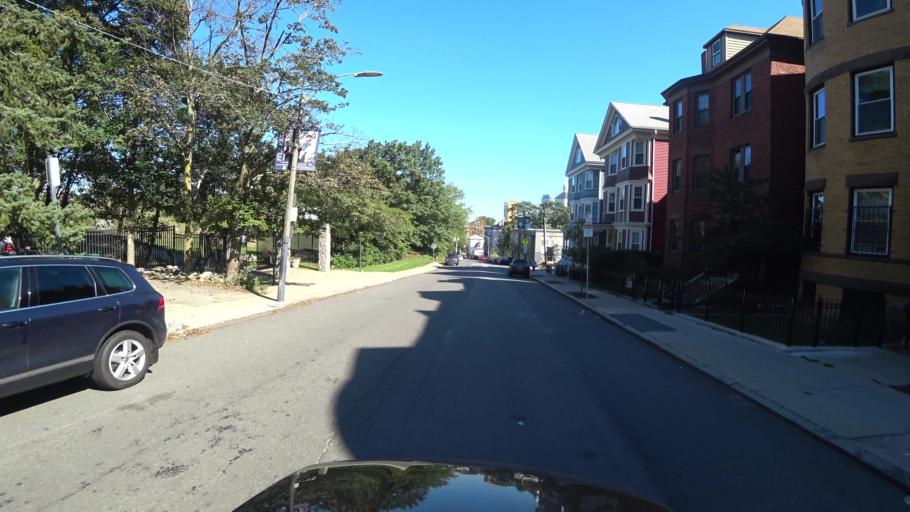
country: US
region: Massachusetts
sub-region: Norfolk County
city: Brookline
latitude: 42.3313
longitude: -71.1025
